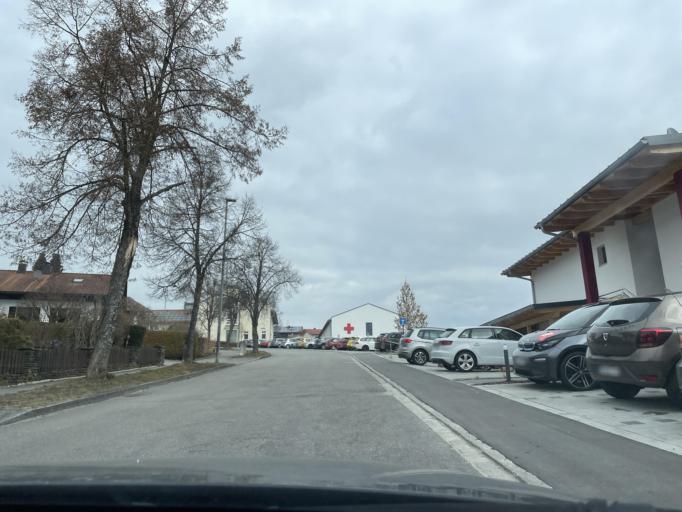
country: DE
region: Bavaria
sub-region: Lower Bavaria
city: Viechtach
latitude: 49.0849
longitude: 12.8782
